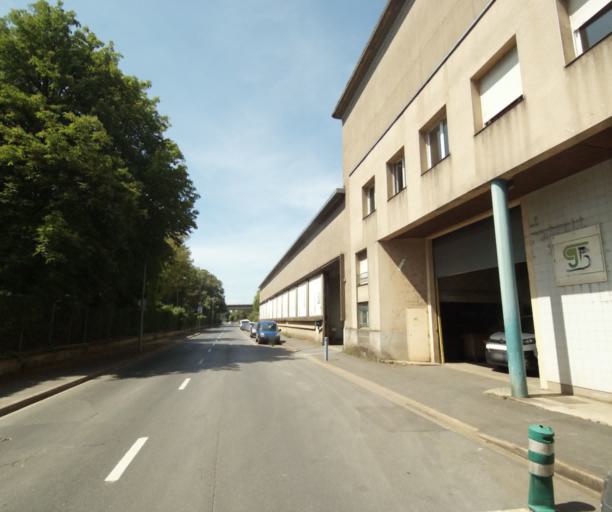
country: FR
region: Champagne-Ardenne
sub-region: Departement des Ardennes
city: Charleville-Mezieres
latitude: 49.7679
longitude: 4.7113
